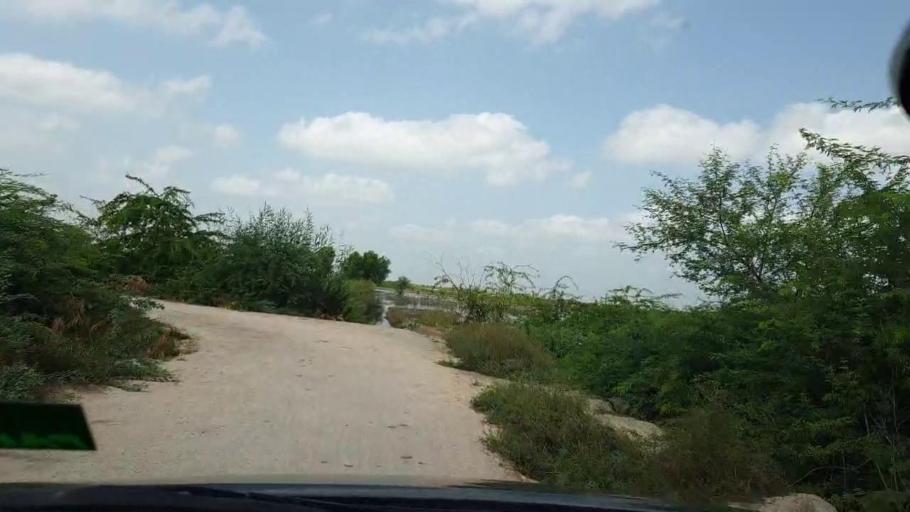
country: PK
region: Sindh
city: Kadhan
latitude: 24.5768
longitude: 69.1477
